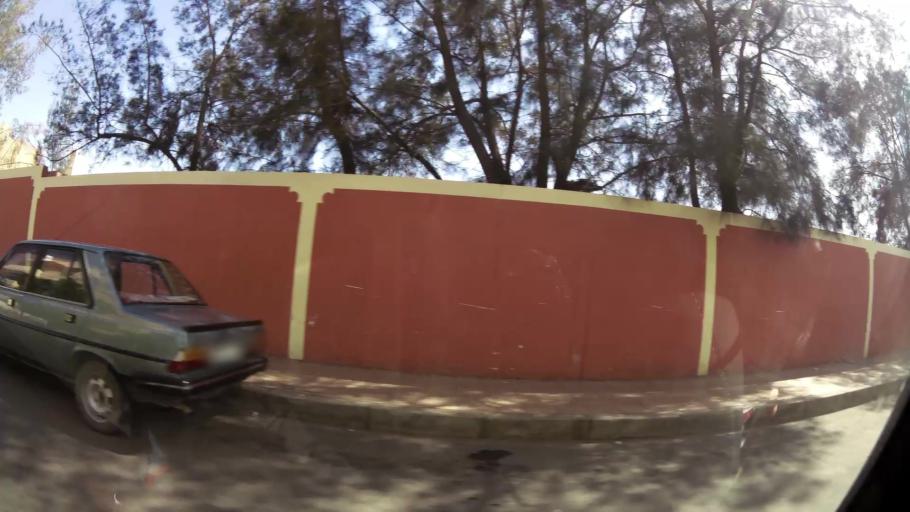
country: MA
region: Souss-Massa-Draa
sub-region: Inezgane-Ait Mellou
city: Inezgane
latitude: 30.3541
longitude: -9.5389
